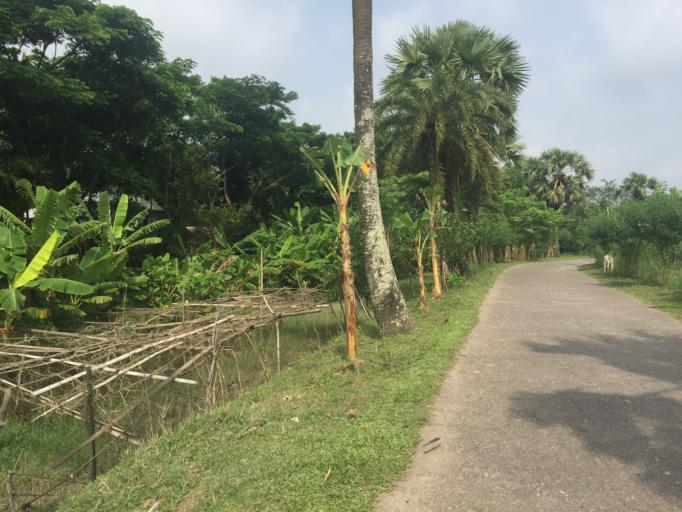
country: BD
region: Barisal
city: Mathba
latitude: 22.2554
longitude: 89.9120
